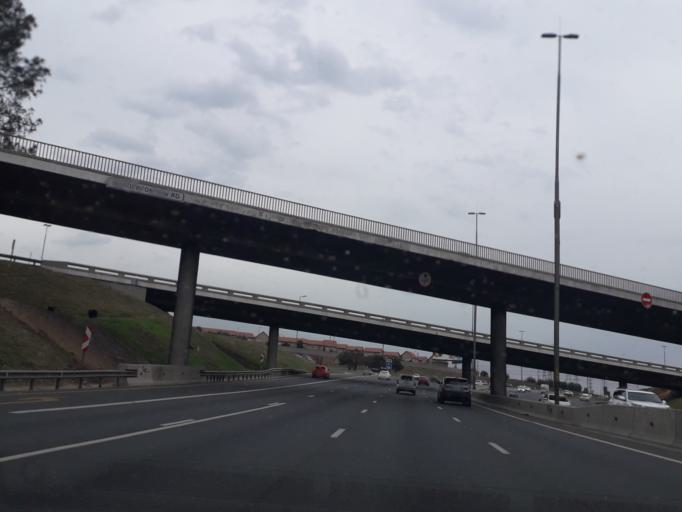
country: ZA
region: Gauteng
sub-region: City of Johannesburg Metropolitan Municipality
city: Modderfontein
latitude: -26.1211
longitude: 28.1354
